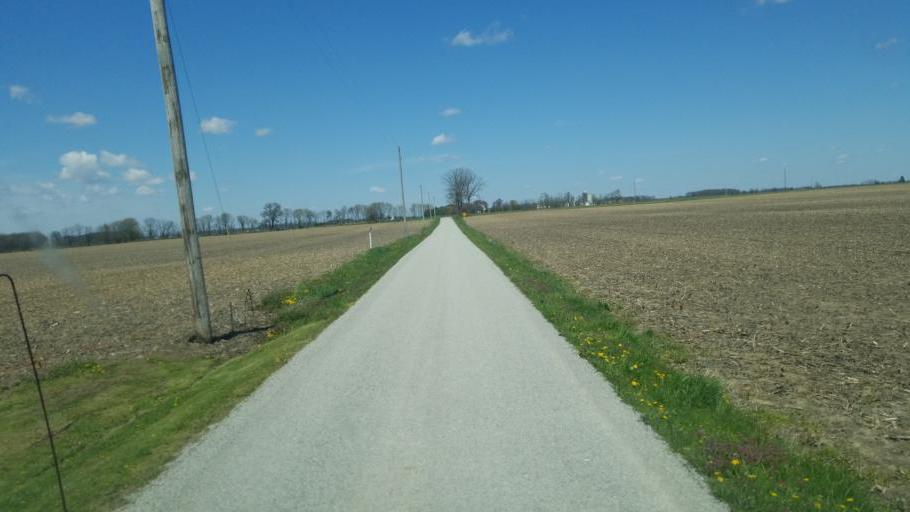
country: US
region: Ohio
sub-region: Marion County
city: Prospect
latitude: 40.3905
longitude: -83.1300
